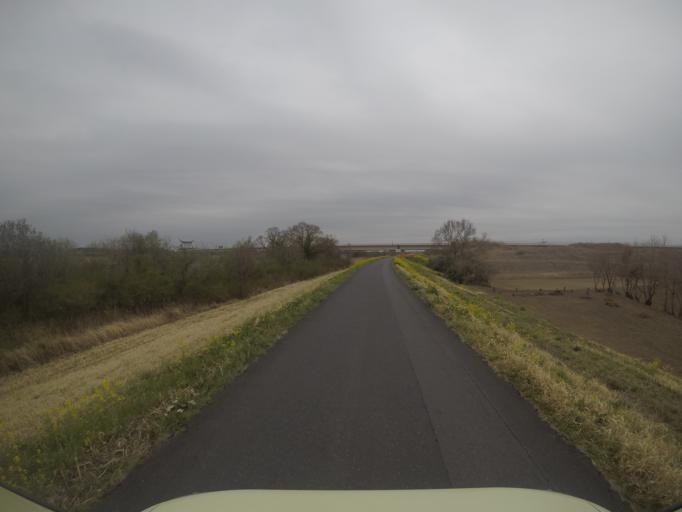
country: JP
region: Ibaraki
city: Ishige
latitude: 36.0821
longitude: 140.0020
